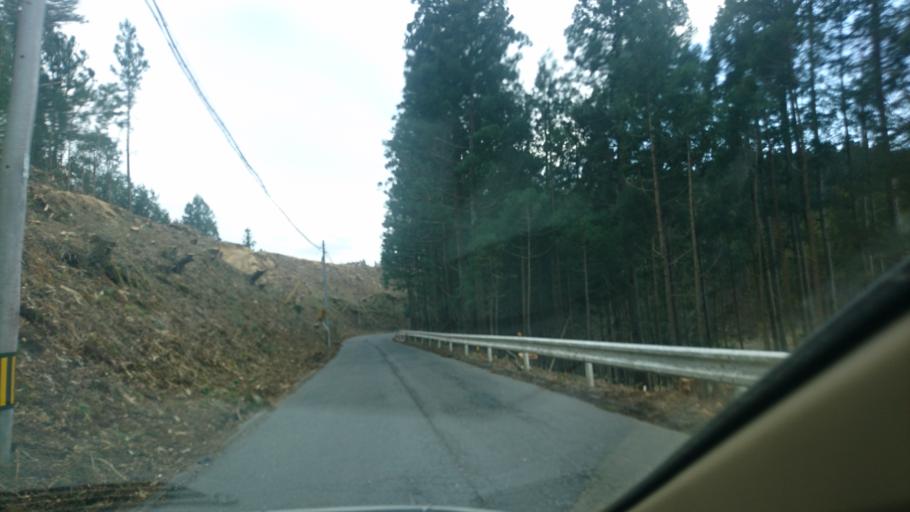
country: JP
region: Miyagi
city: Furukawa
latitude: 38.7251
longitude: 140.8320
